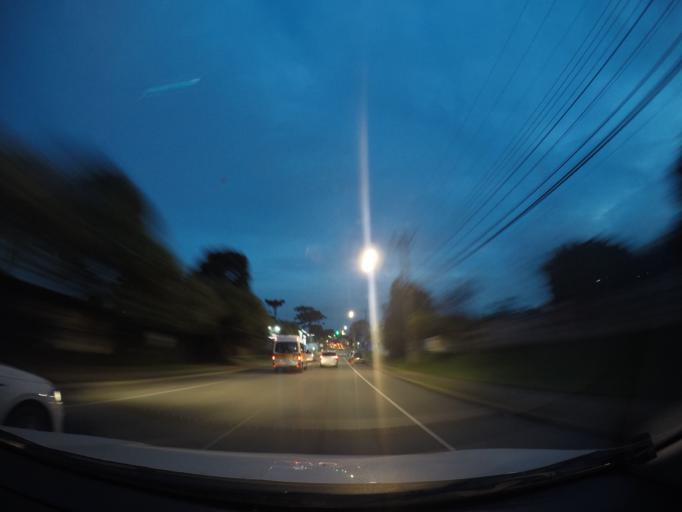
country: BR
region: Parana
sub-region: Curitiba
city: Curitiba
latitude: -25.4152
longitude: -49.2815
